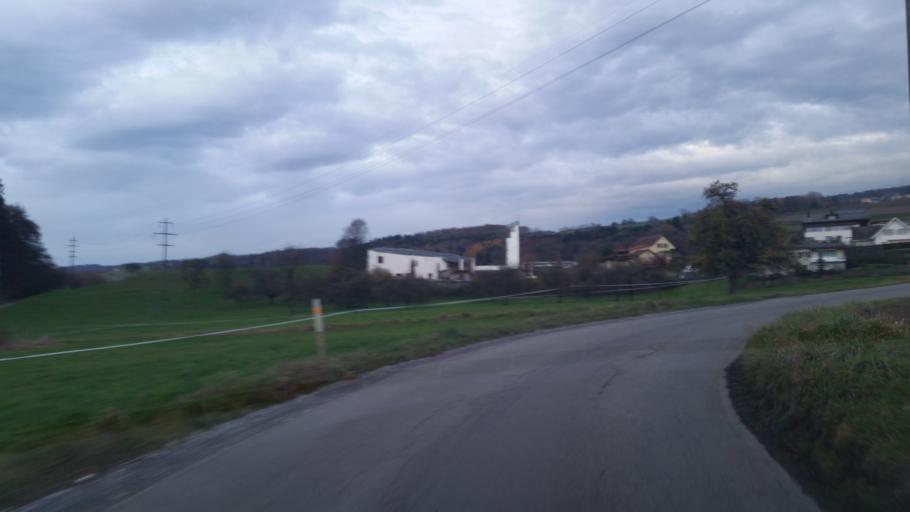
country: CH
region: Aargau
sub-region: Bezirk Baden
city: Kunten
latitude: 47.3883
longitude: 8.3250
